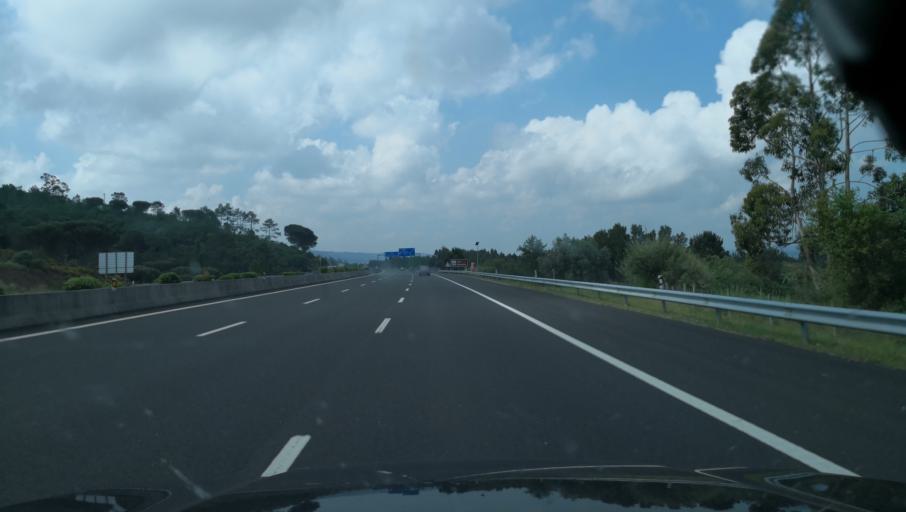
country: PT
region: Leiria
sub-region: Nazare
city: Nazare
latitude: 39.5181
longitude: -9.0864
